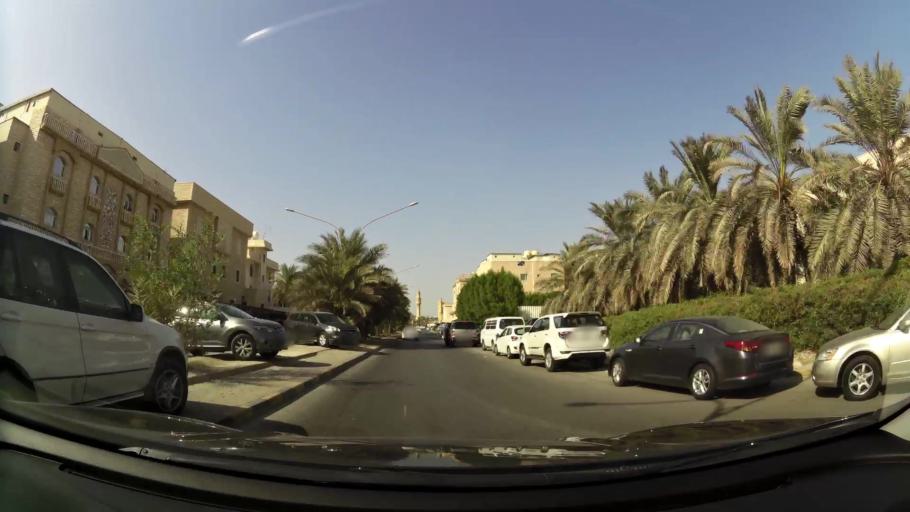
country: KW
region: Muhafazat Hawalli
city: Salwa
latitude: 29.2931
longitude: 48.0774
